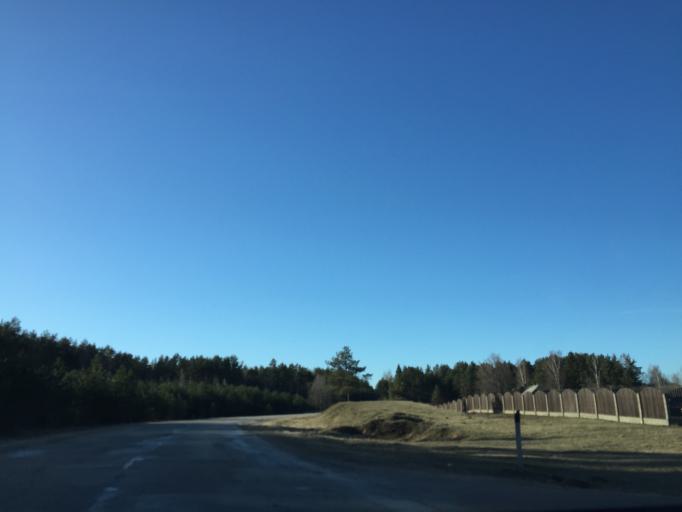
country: LV
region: Ropazu
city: Ropazi
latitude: 56.9430
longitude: 24.6035
